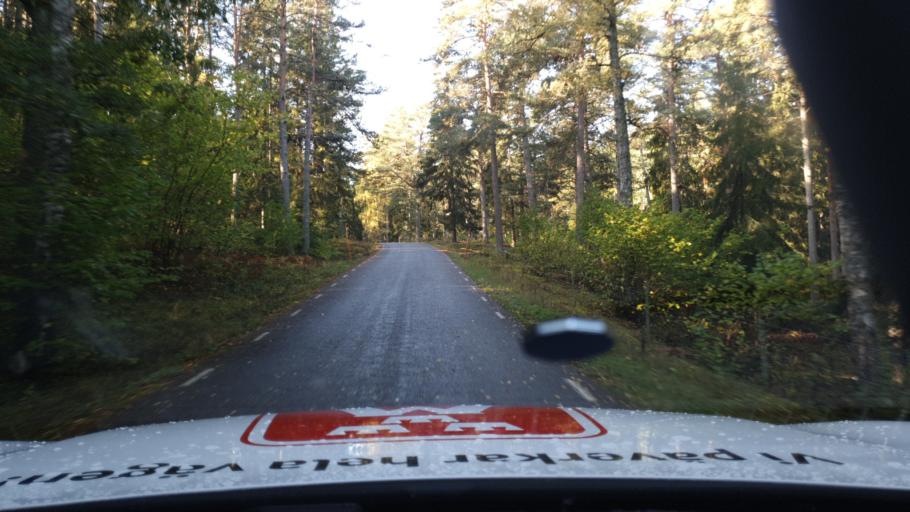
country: SE
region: Kalmar
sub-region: Vasterviks Kommun
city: Forserum
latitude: 57.9907
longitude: 16.5880
